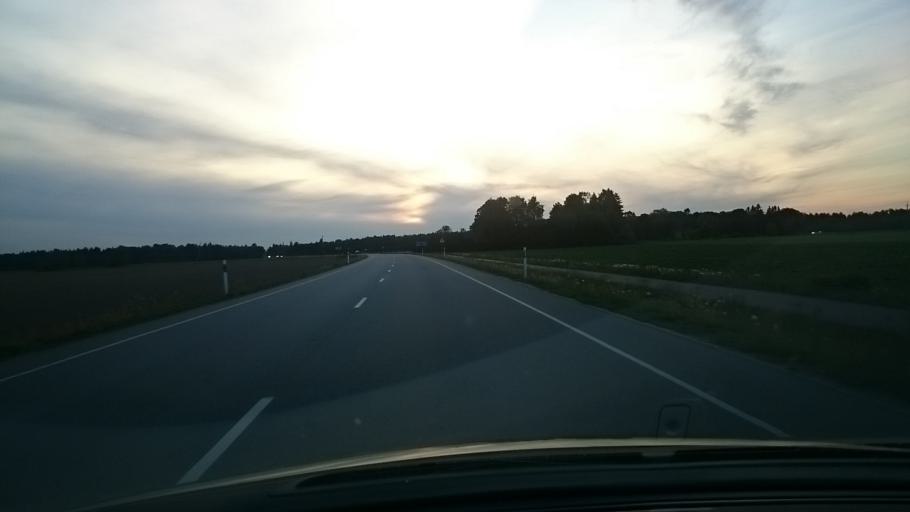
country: EE
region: Jaervamaa
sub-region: Paide linn
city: Paide
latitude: 58.7593
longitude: 25.5548
